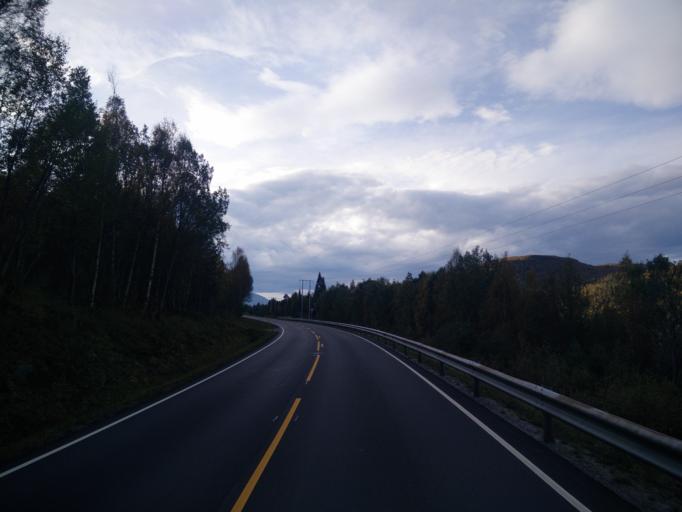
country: NO
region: More og Romsdal
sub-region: Gjemnes
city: Batnfjordsora
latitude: 62.8494
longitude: 7.5973
